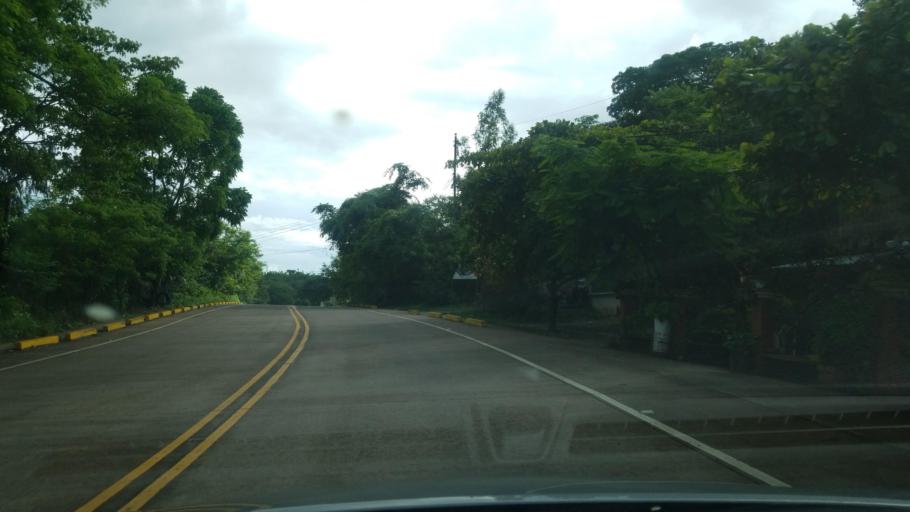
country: HN
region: Copan
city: Copan
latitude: 14.8423
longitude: -89.1723
